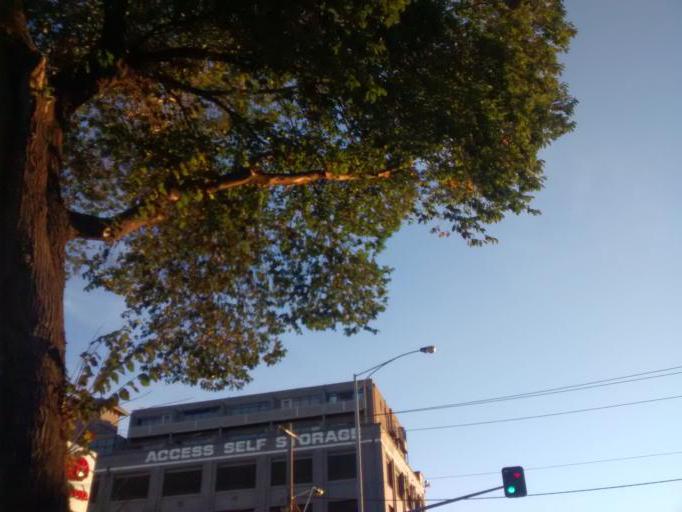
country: AU
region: Victoria
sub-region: Port Phillip
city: Port Melbourne
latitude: -37.8287
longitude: 144.9488
